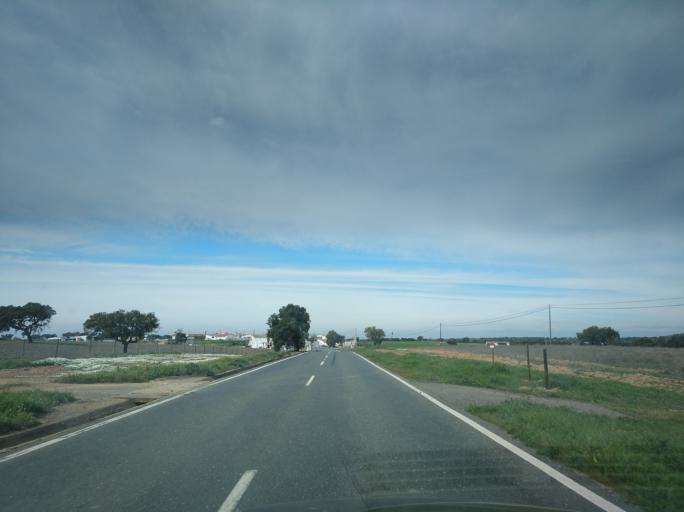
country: PT
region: Beja
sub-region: Mertola
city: Mertola
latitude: 37.7583
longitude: -7.8116
